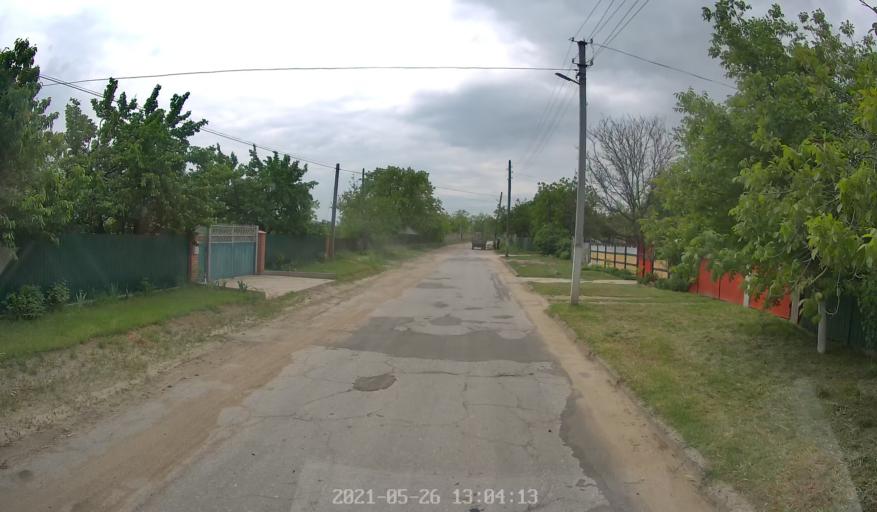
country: MD
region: Hincesti
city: Dancu
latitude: 46.7595
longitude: 28.3408
